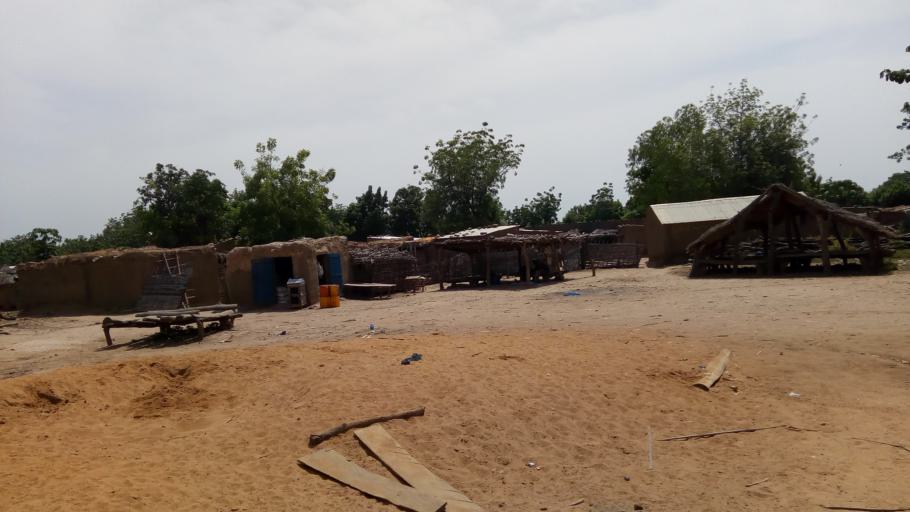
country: ML
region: Kayes
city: Kita
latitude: 13.4001
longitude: -8.8607
